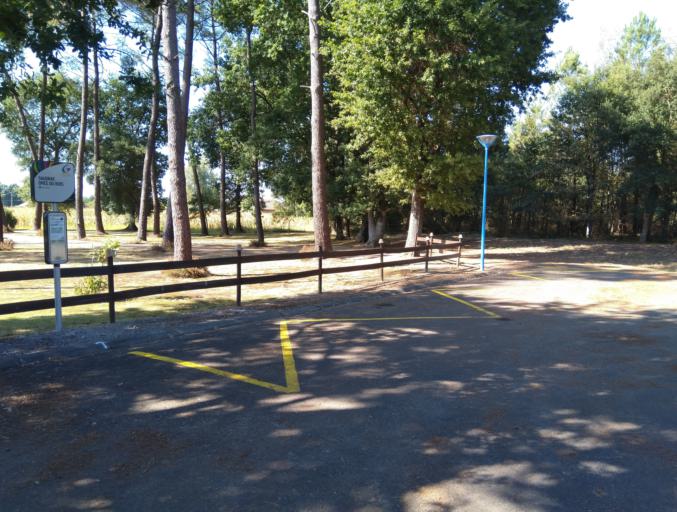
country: FR
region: Aquitaine
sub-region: Departement des Landes
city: Saugnac-et-Cambran
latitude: 43.6900
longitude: -0.9856
